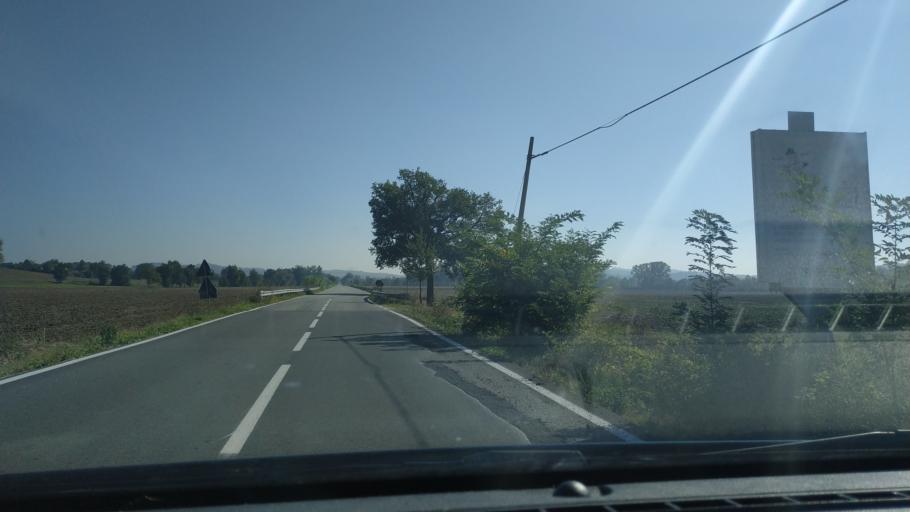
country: IT
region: Piedmont
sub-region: Provincia di Alessandria
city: Serralunga di Crea
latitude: 45.1132
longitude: 8.2888
